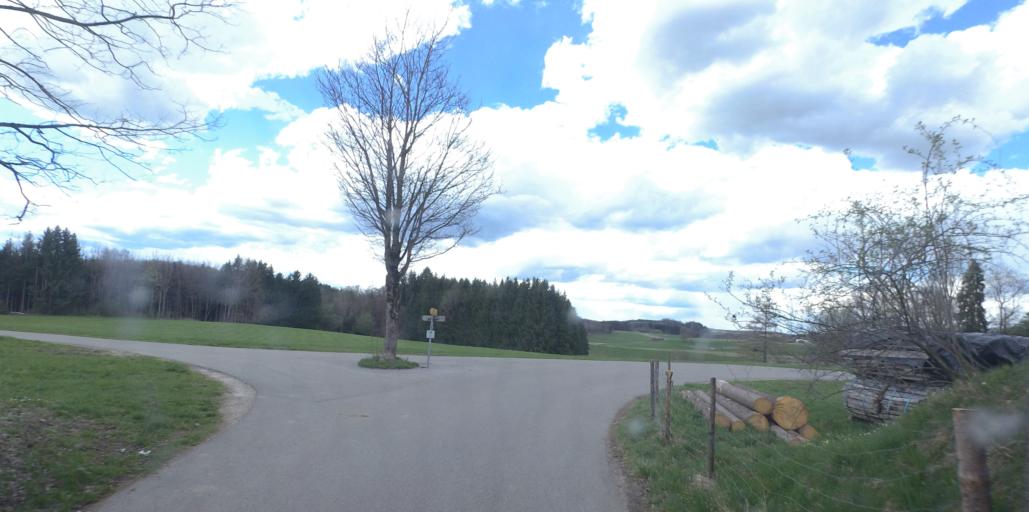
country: DE
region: Bavaria
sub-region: Upper Bavaria
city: Vachendorf
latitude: 47.8350
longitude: 12.6042
